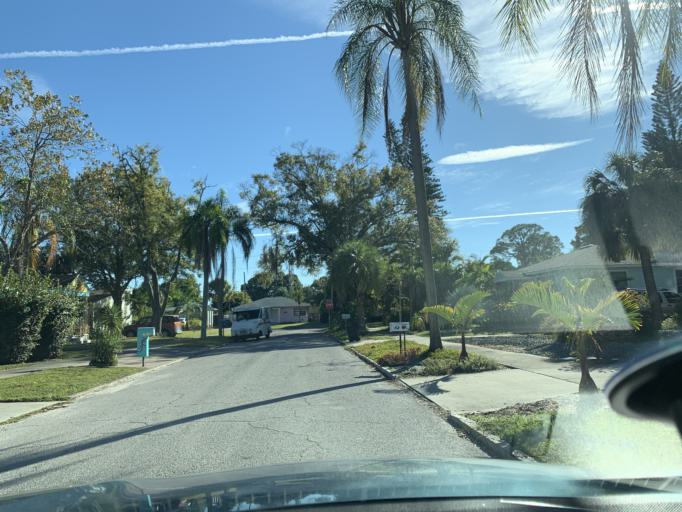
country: US
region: Florida
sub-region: Pinellas County
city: Gulfport
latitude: 27.7417
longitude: -82.6989
